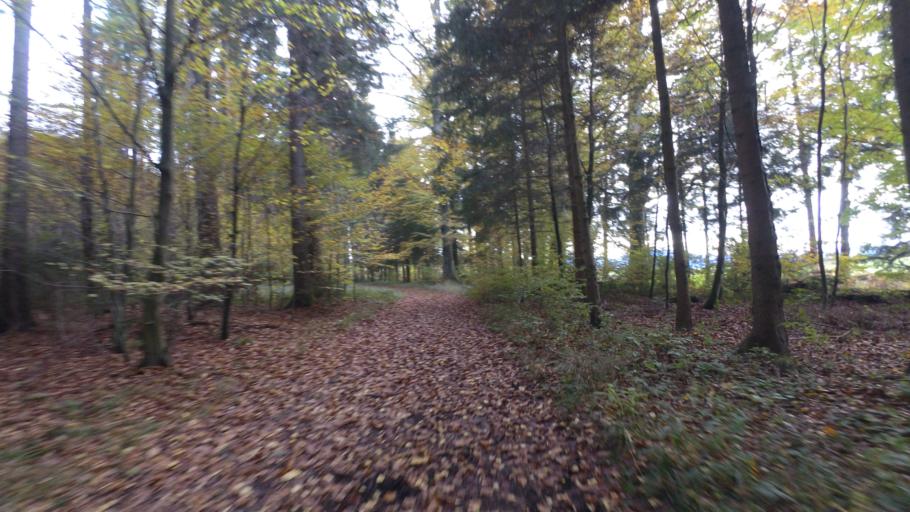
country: DE
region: Bavaria
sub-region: Upper Bavaria
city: Traunreut
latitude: 47.9340
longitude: 12.5758
